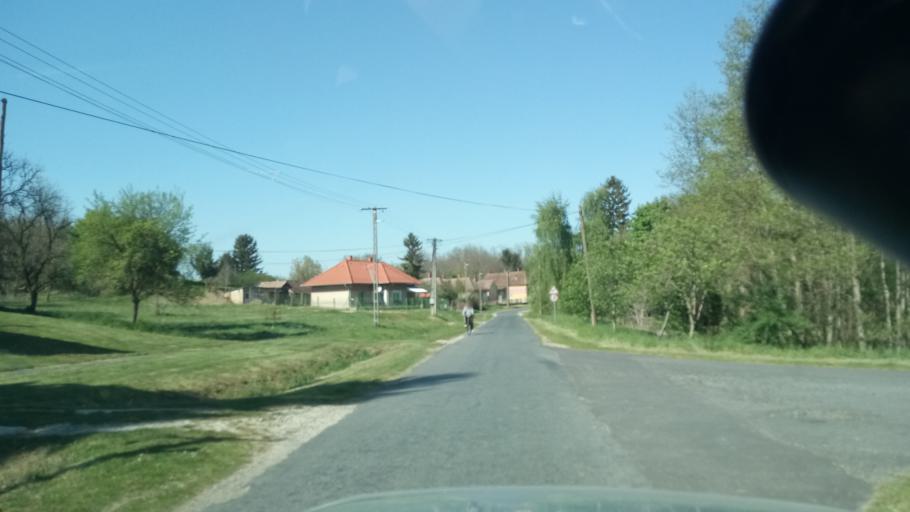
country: HU
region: Zala
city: Sarmellek
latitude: 46.6999
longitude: 17.1036
